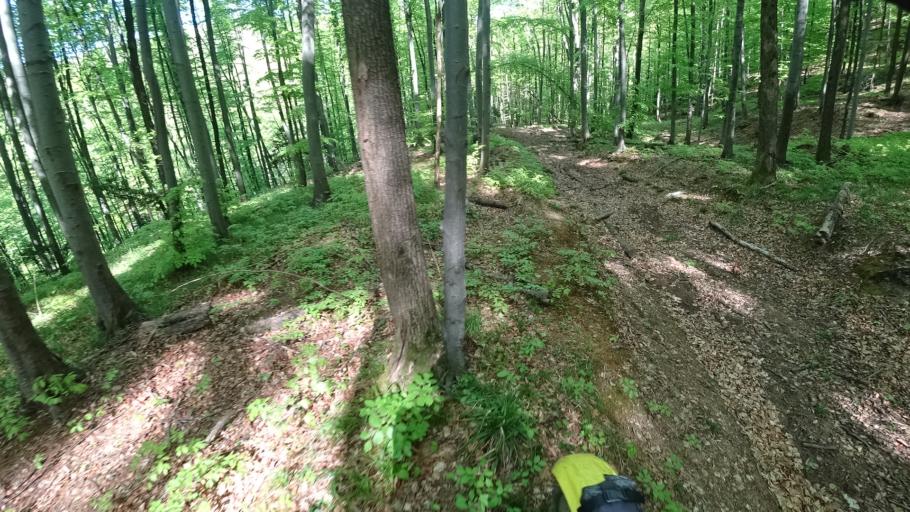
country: HR
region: Zagrebacka
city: Jablanovec
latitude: 45.8900
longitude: 15.8995
